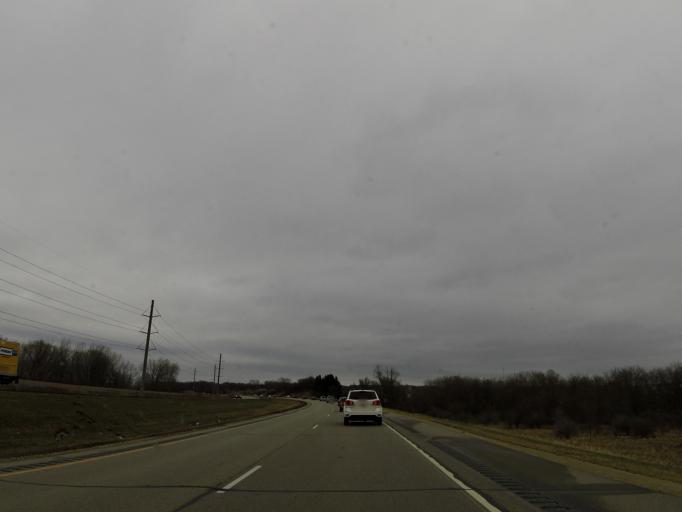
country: US
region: Minnesota
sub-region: Olmsted County
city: Byron
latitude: 44.0269
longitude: -92.5710
